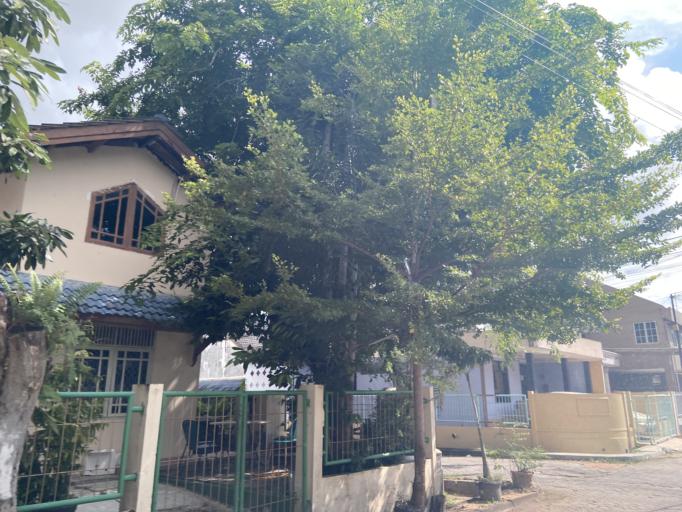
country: SG
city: Singapore
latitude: 1.1217
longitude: 104.0254
